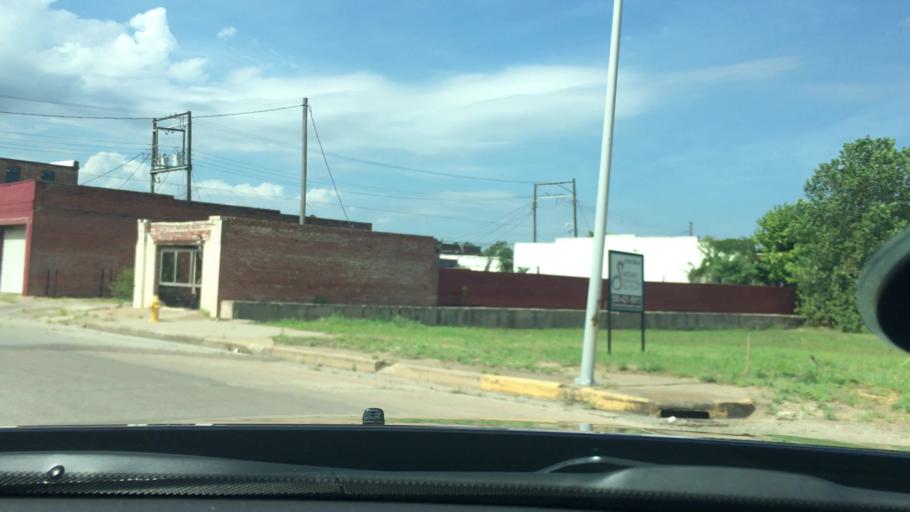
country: US
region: Oklahoma
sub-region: Pontotoc County
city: Ada
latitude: 34.7756
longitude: -96.6802
